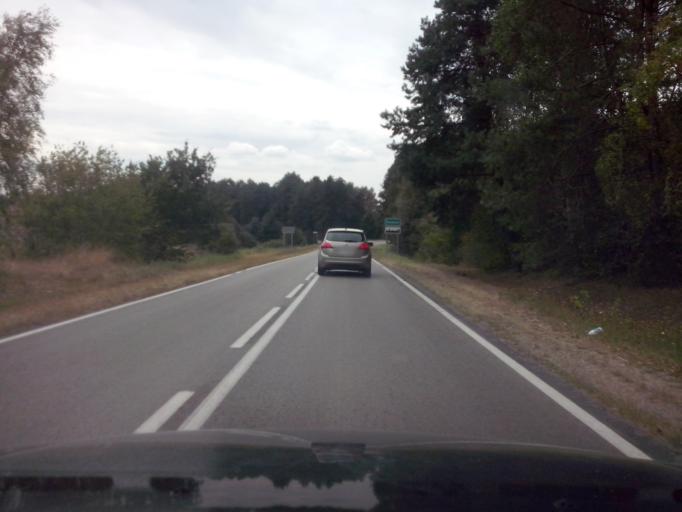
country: PL
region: Swietokrzyskie
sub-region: Powiat kielecki
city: Rakow
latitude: 50.7134
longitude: 21.0600
